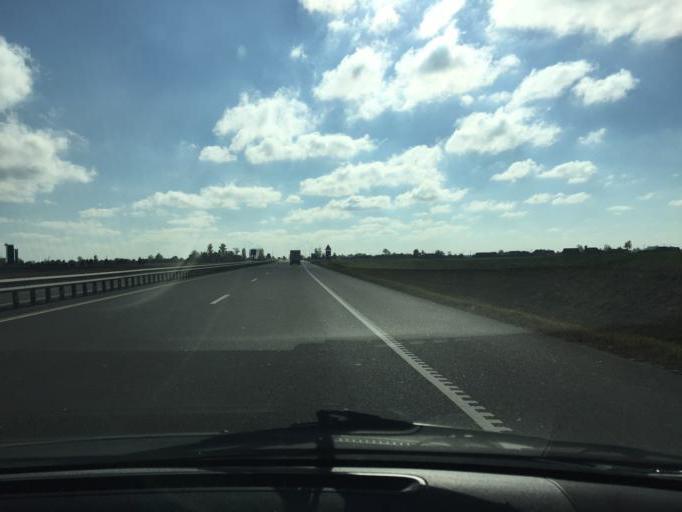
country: BY
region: Minsk
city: Slutsk
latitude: 53.1114
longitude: 27.5670
